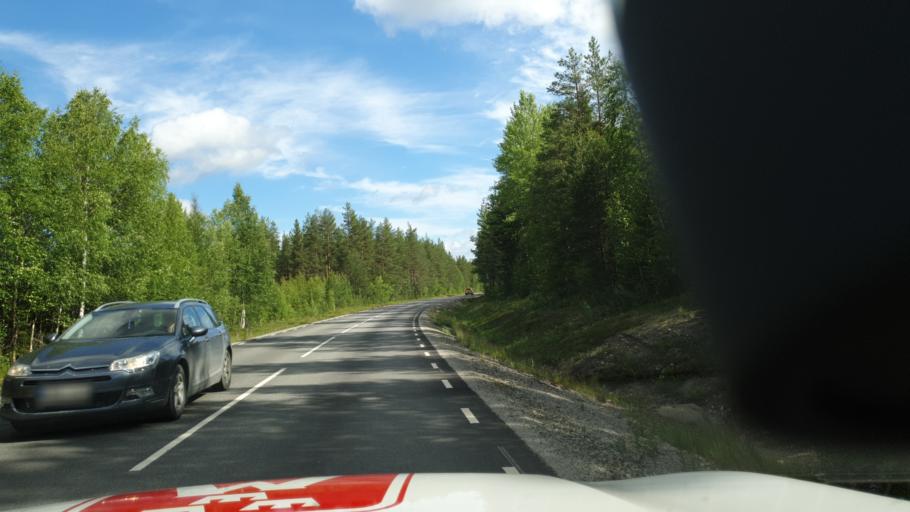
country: SE
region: Vaesterbotten
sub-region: Norsjo Kommun
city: Norsjoe
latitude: 64.6253
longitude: 19.2850
